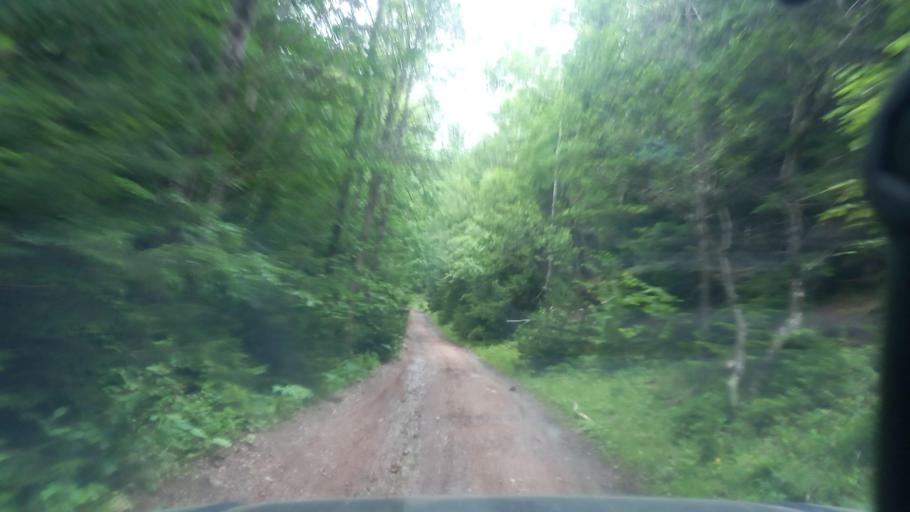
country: RU
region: Karachayevo-Cherkesiya
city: Kurdzhinovo
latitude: 43.8108
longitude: 40.8691
